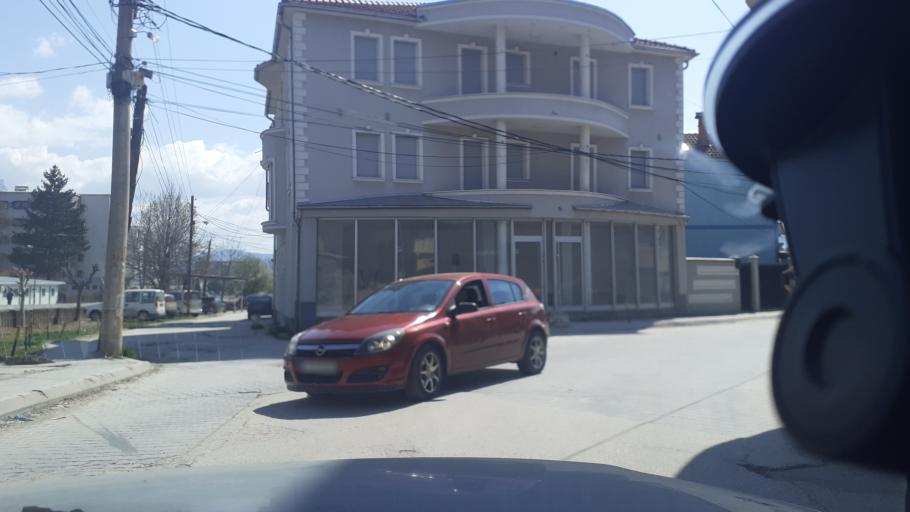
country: MK
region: Tetovo
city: Tetovo
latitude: 42.0051
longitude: 20.9693
